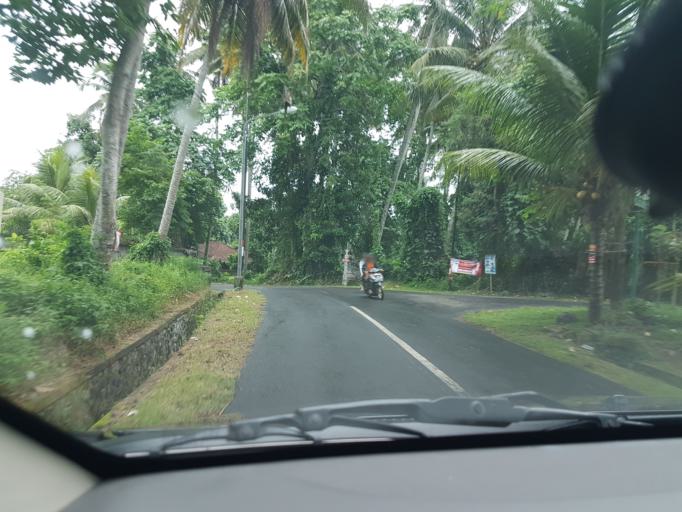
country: ID
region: Bali
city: Banjar Tebongkang
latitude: -8.5300
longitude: 115.2375
